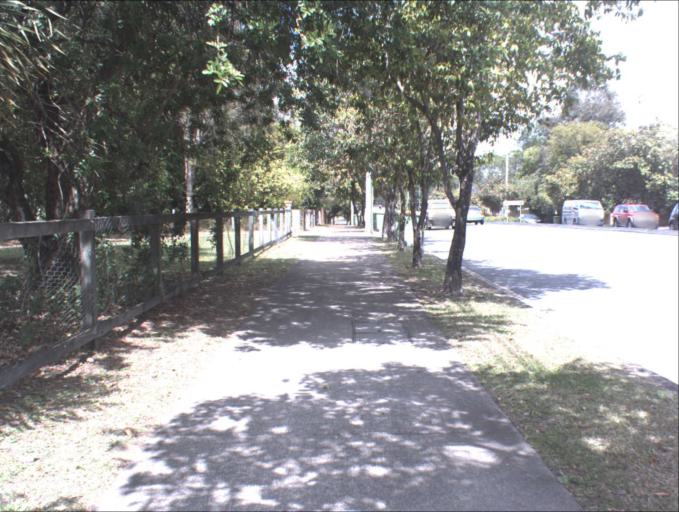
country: AU
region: Queensland
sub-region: Logan
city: Waterford West
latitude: -27.6765
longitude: 153.1382
